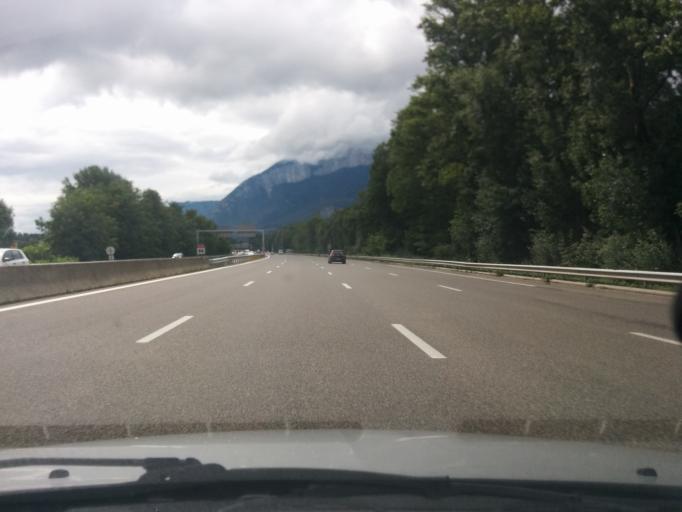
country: FR
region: Rhone-Alpes
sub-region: Departement de l'Isere
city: Voreppe
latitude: 45.2909
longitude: 5.6200
